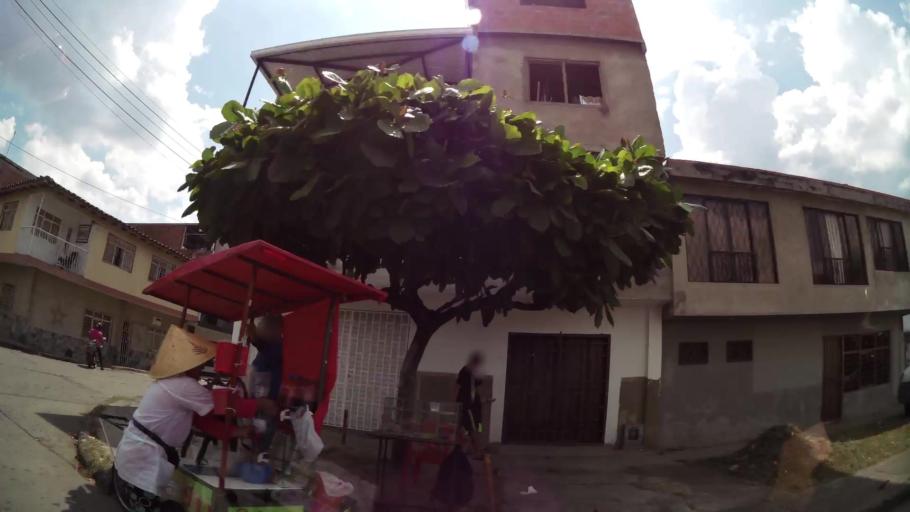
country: CO
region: Valle del Cauca
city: Cali
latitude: 3.4641
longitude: -76.5035
